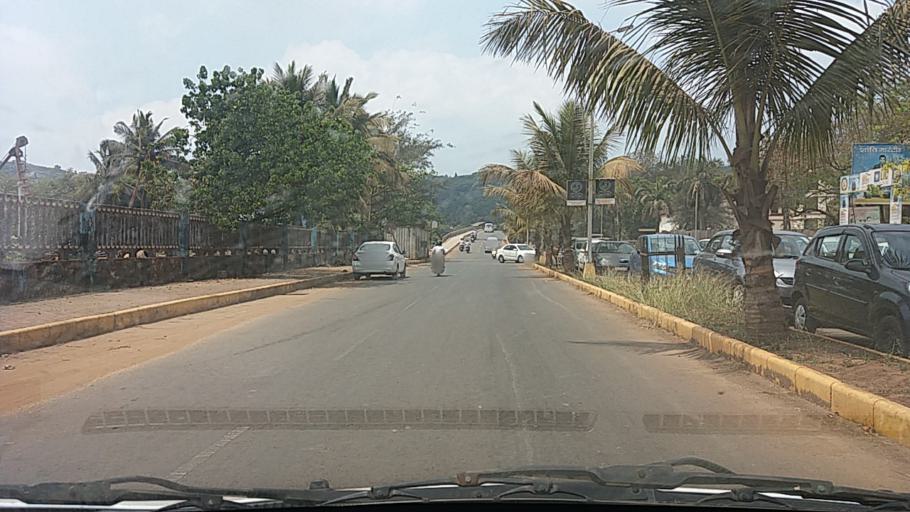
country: IN
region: Goa
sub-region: North Goa
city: Panaji
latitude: 15.4925
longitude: 73.8345
